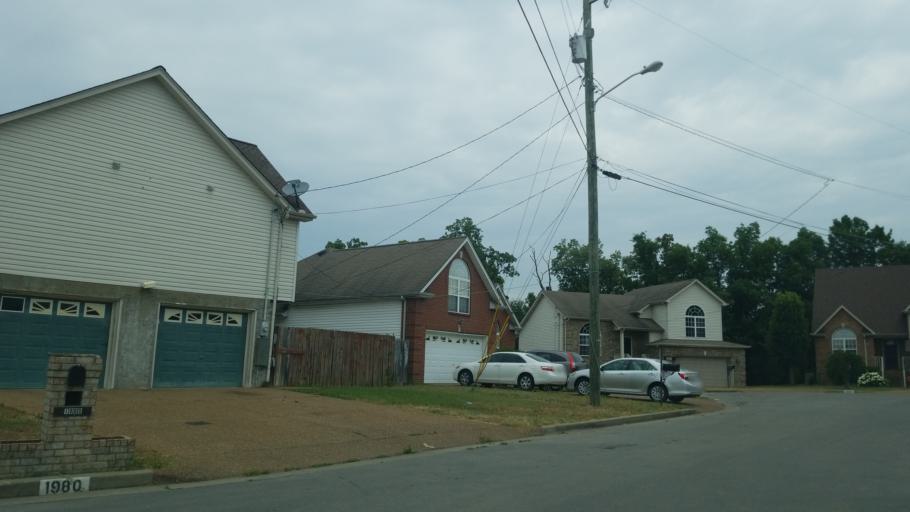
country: US
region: Tennessee
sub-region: Rutherford County
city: La Vergne
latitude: 36.0498
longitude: -86.5850
